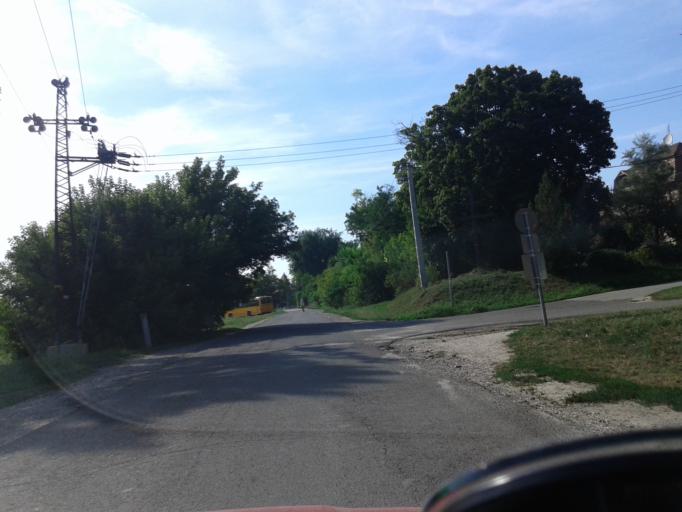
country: HU
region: Pest
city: Godollo
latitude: 47.5974
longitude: 19.3959
